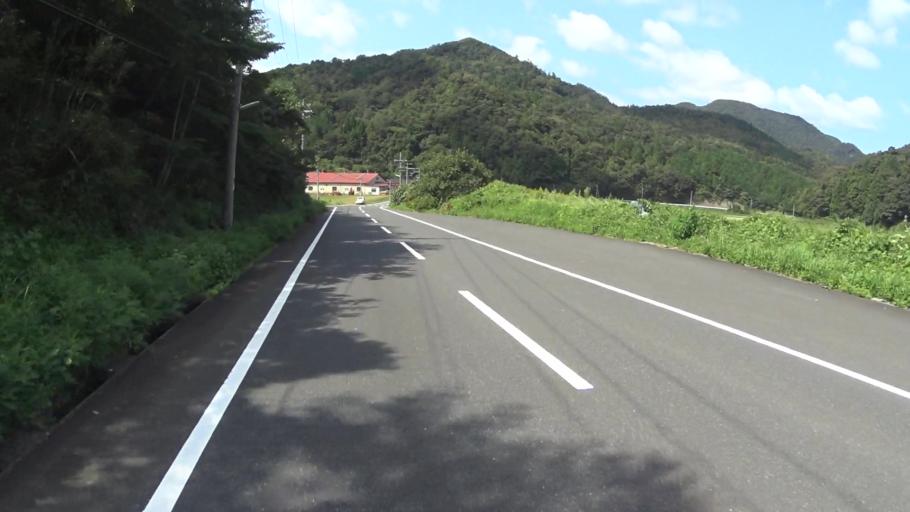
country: JP
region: Kyoto
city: Miyazu
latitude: 35.7090
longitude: 135.2529
